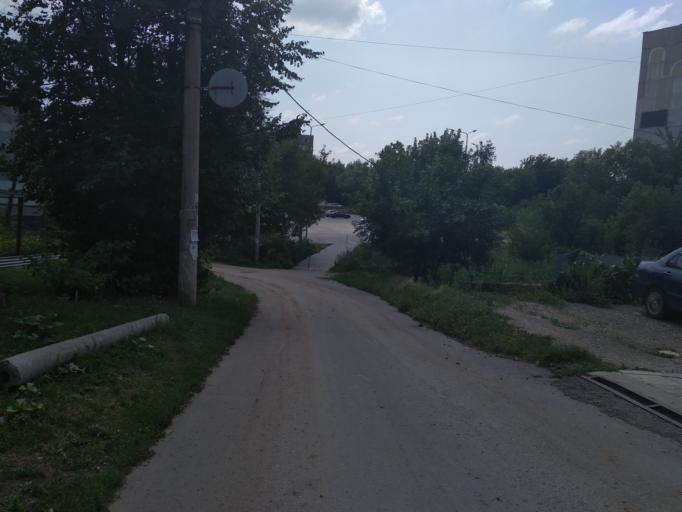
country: RU
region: Tula
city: Mendeleyevskiy
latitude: 54.1606
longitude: 37.6041
